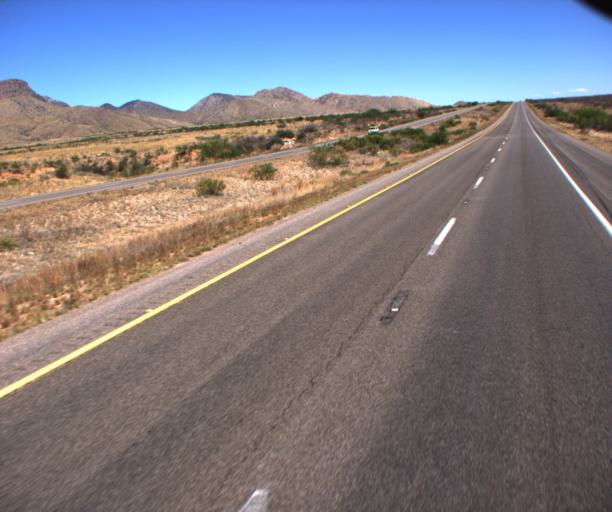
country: US
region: Arizona
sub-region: Cochise County
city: Huachuca City
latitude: 31.7895
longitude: -110.3499
